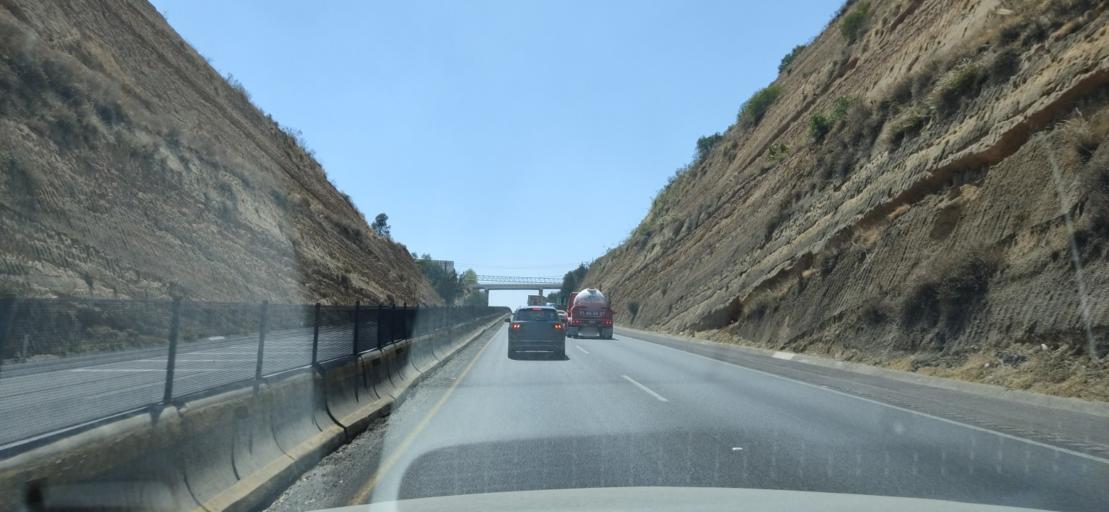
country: MX
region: Mexico
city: Ciudad Lopez Mateos
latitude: 19.5767
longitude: -99.2698
